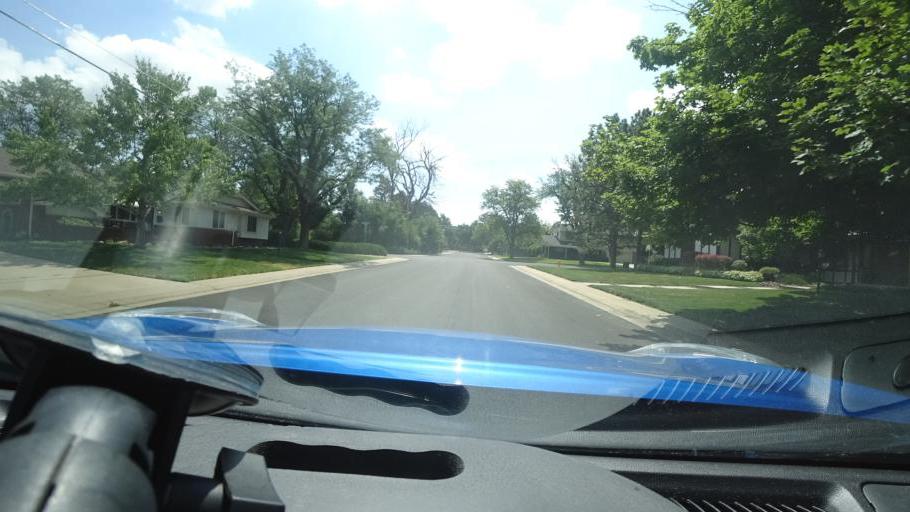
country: US
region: Colorado
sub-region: Adams County
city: Aurora
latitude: 39.7214
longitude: -104.8528
